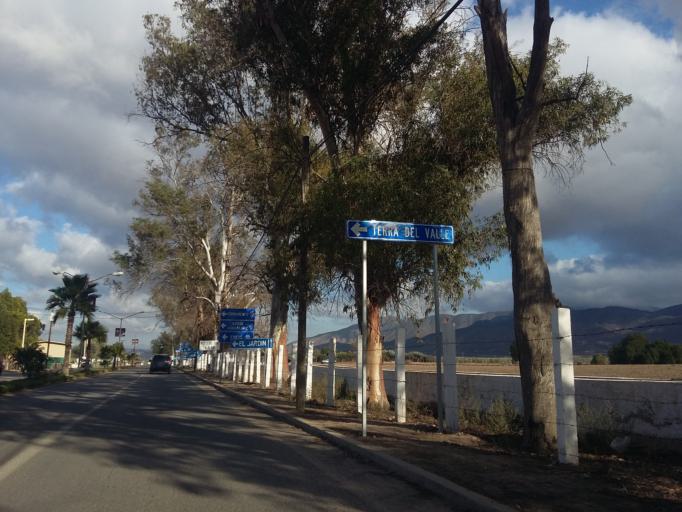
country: MX
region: Baja California
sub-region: Ensenada
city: Rancho Verde
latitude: 32.0771
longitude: -116.6207
